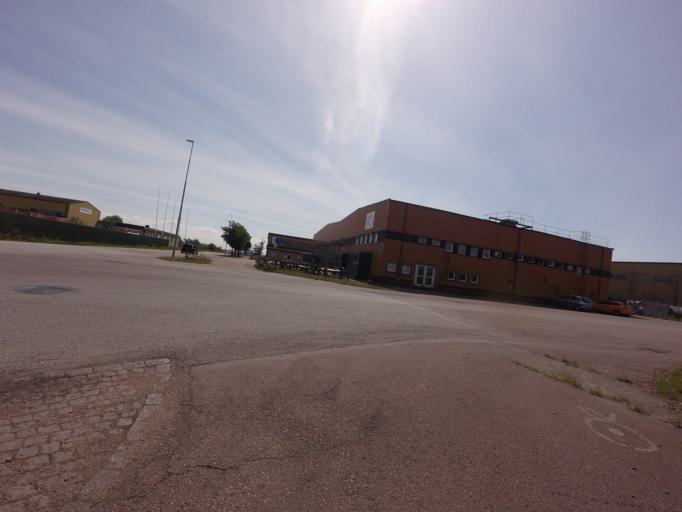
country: SE
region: Skane
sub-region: Landskrona
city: Landskrona
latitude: 55.8584
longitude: 12.8413
